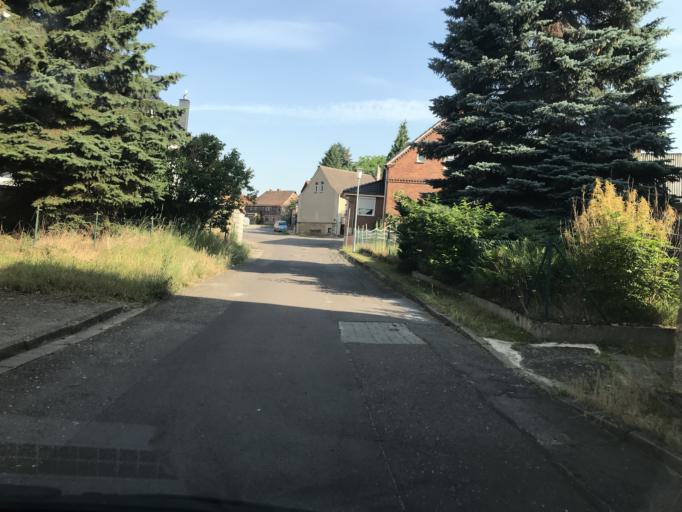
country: DE
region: Saxony-Anhalt
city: Beendorf
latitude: 52.2406
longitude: 11.1356
